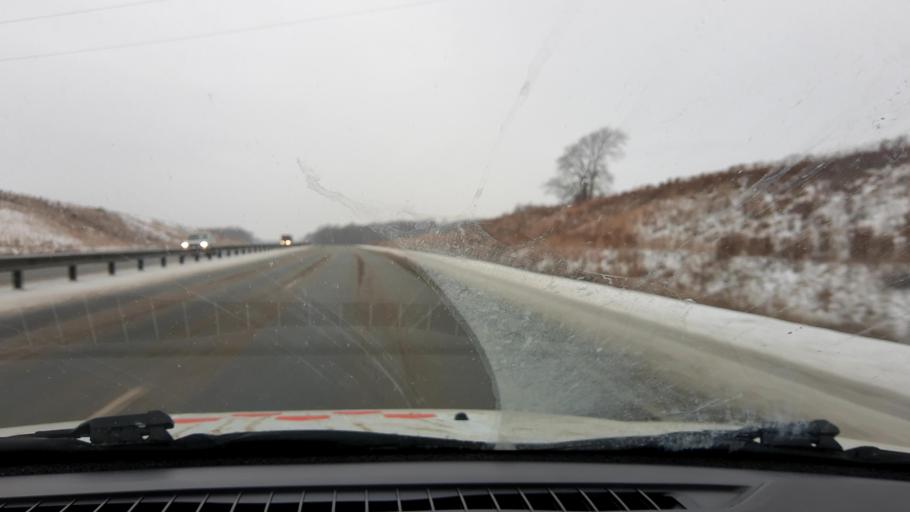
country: RU
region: Nizjnij Novgorod
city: Kstovo
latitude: 56.1003
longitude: 44.0510
